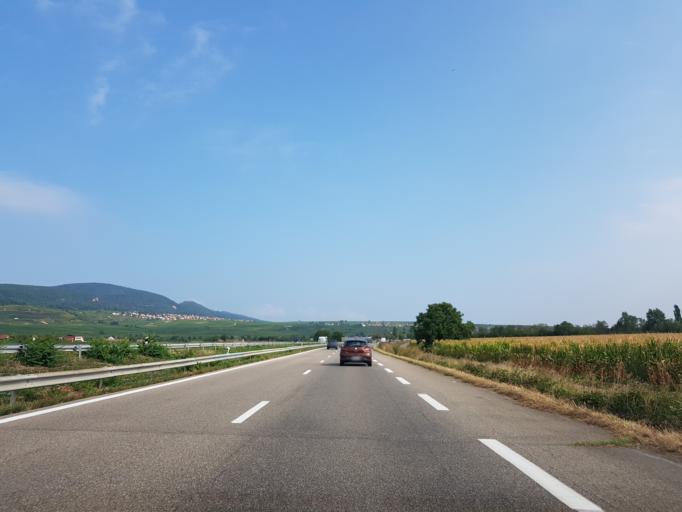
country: FR
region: Alsace
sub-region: Departement du Haut-Rhin
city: Pfaffenheim
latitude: 47.9933
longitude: 7.2940
